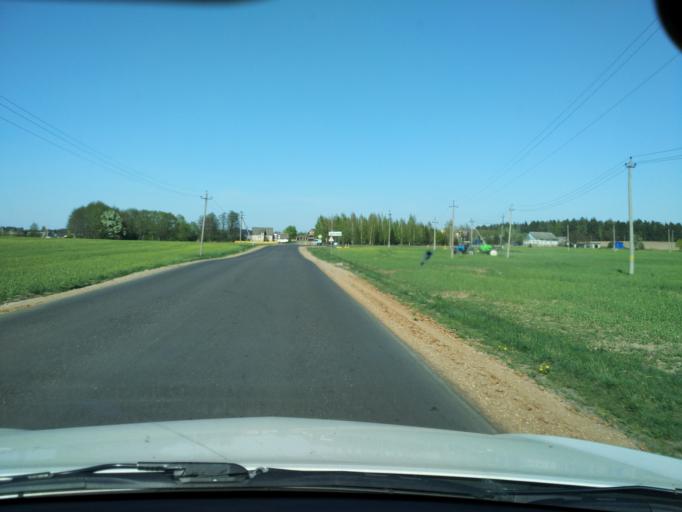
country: BY
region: Minsk
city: Lyeskawka
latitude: 54.0089
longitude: 27.7407
